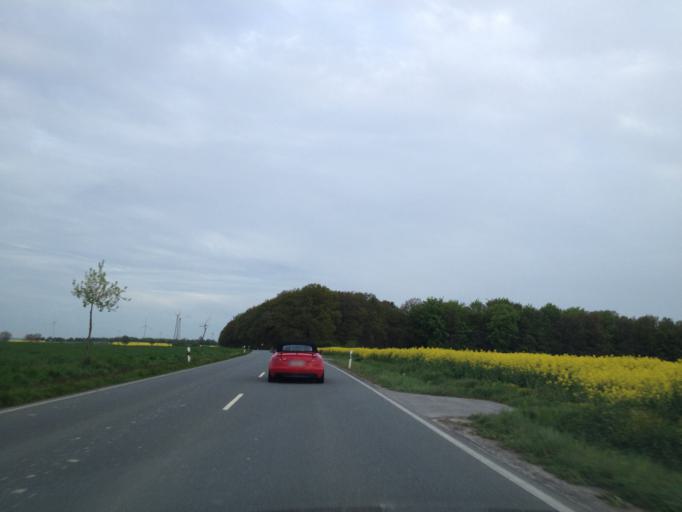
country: DE
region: North Rhine-Westphalia
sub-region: Regierungsbezirk Arnsberg
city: Mohnesee
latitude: 51.5049
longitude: 8.1141
